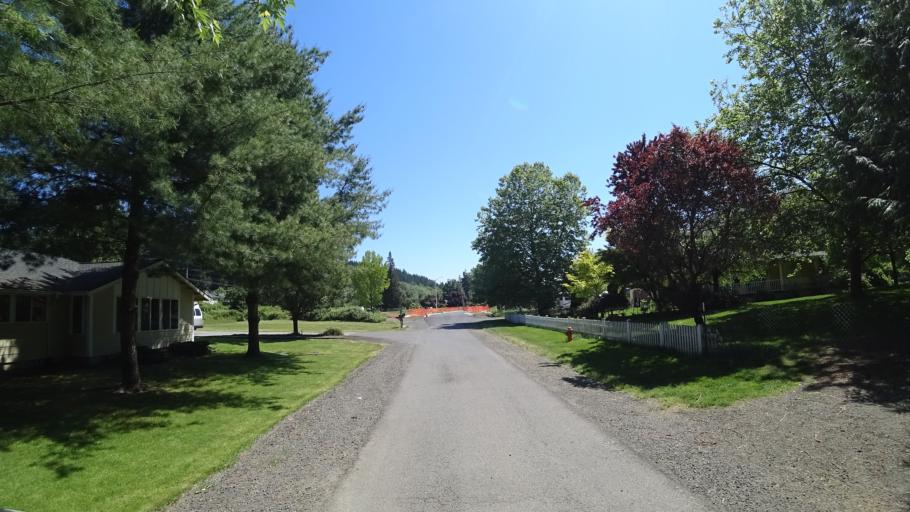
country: US
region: Oregon
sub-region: Clackamas County
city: Happy Valley
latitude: 45.4796
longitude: -122.5169
